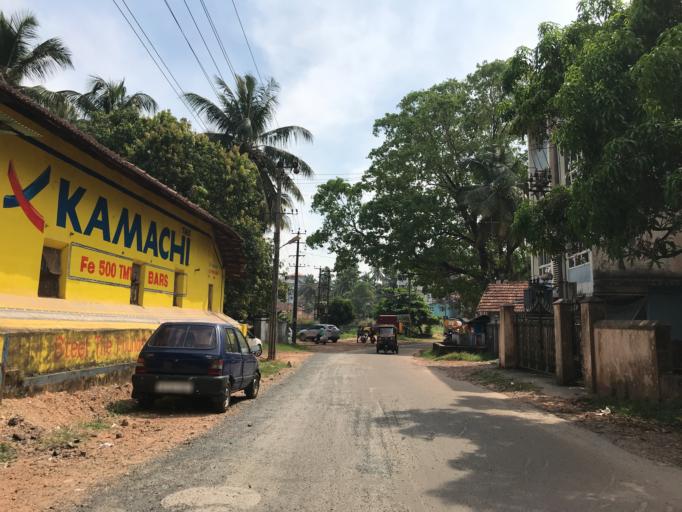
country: IN
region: Karnataka
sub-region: Dakshina Kannada
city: Ullal
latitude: 12.8475
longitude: 74.8495
